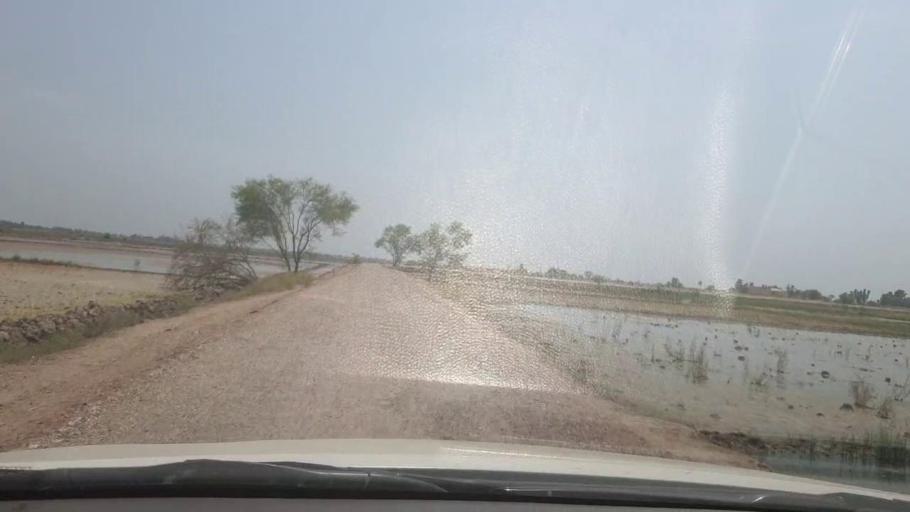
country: PK
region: Sindh
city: Shikarpur
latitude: 28.0383
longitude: 68.5736
